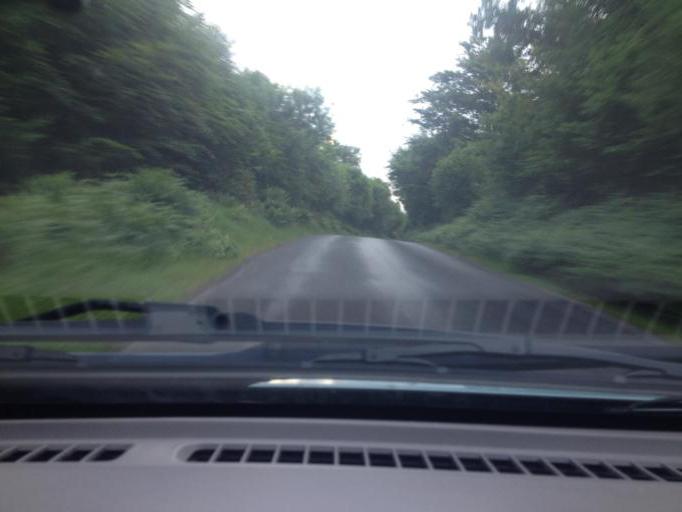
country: IE
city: Ballisodare
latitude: 54.2154
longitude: -8.4806
